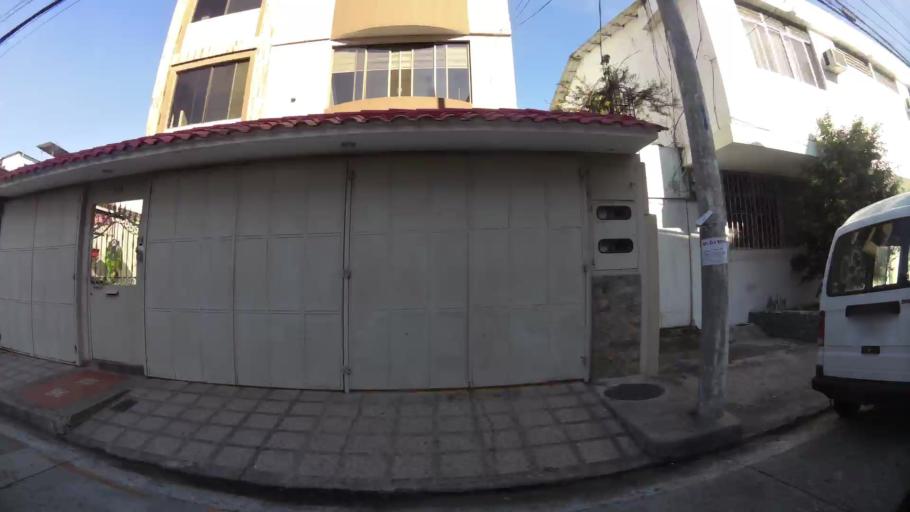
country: EC
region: Guayas
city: Guayaquil
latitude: -2.1721
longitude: -79.8981
